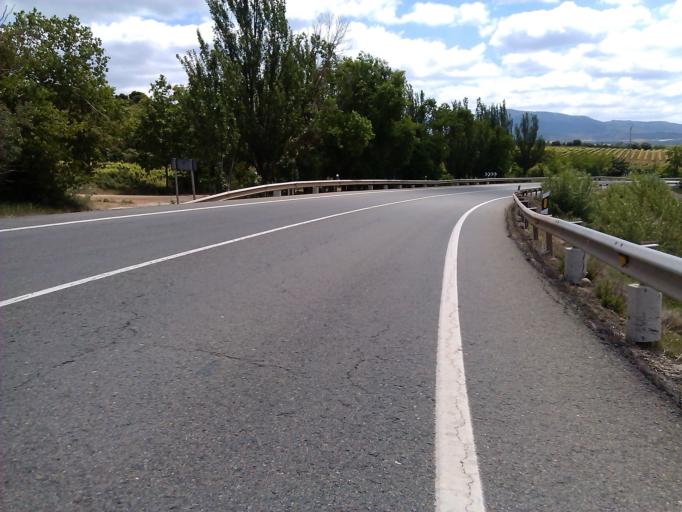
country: ES
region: La Rioja
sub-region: Provincia de La Rioja
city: Ventosa
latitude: 42.4123
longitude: -2.6500
